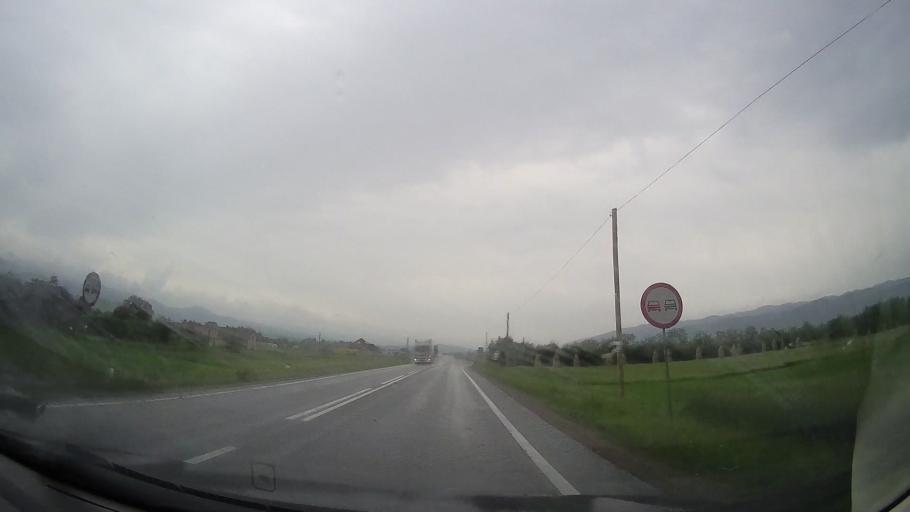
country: RO
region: Caras-Severin
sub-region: Comuna Bucosnita
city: Bucosnita
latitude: 45.3046
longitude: 22.2802
